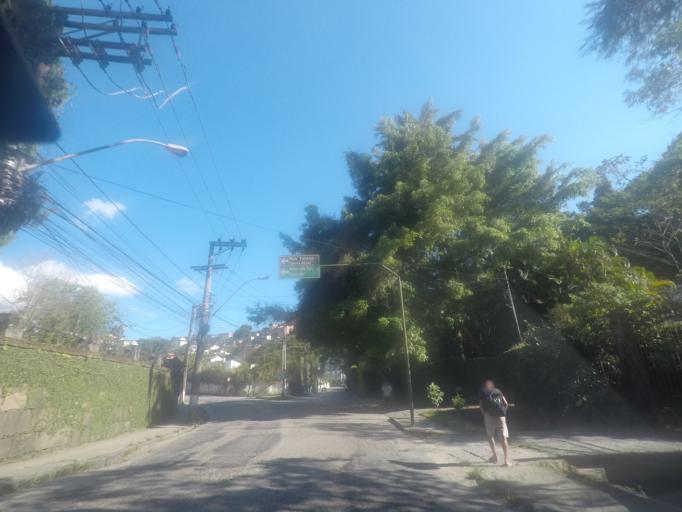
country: BR
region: Rio de Janeiro
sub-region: Petropolis
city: Petropolis
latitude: -22.5260
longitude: -43.1822
